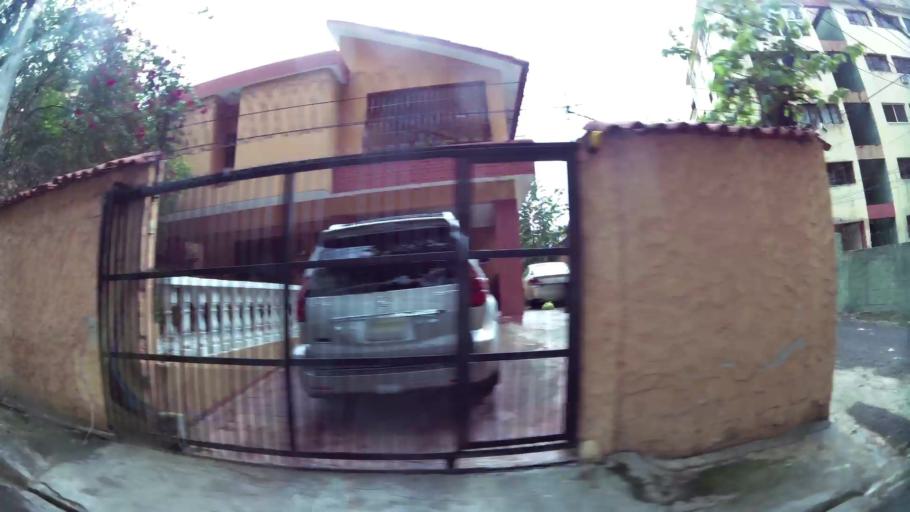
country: DO
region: Nacional
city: La Agustina
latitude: 18.5058
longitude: -69.9358
